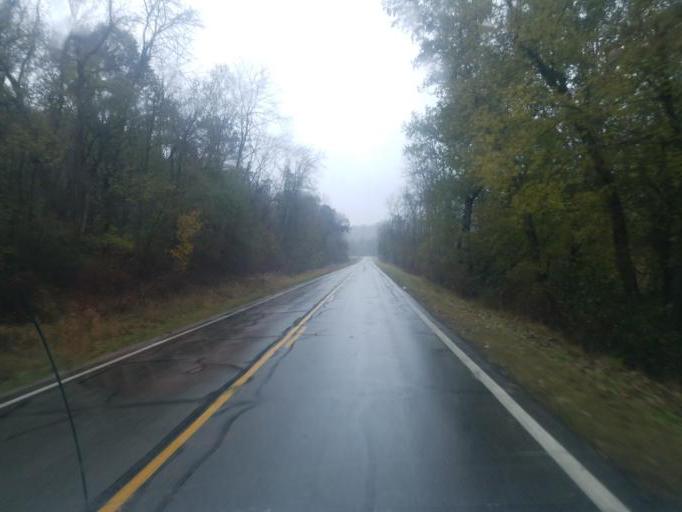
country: US
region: Ohio
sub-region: Muskingum County
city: South Zanesville
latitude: 39.7911
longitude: -81.9019
